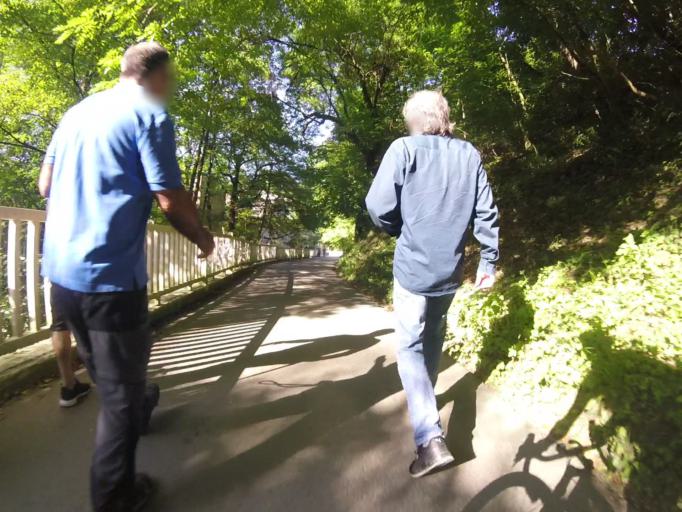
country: ES
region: Basque Country
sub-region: Provincia de Guipuzcoa
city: Pasaia
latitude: 43.3110
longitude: -1.9236
